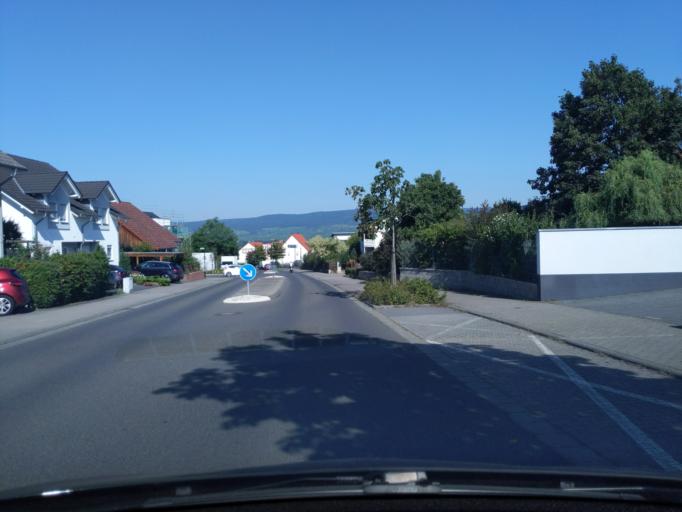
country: DE
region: Rheinland-Pfalz
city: Nieder-Ingelheim
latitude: 49.9814
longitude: 8.0769
